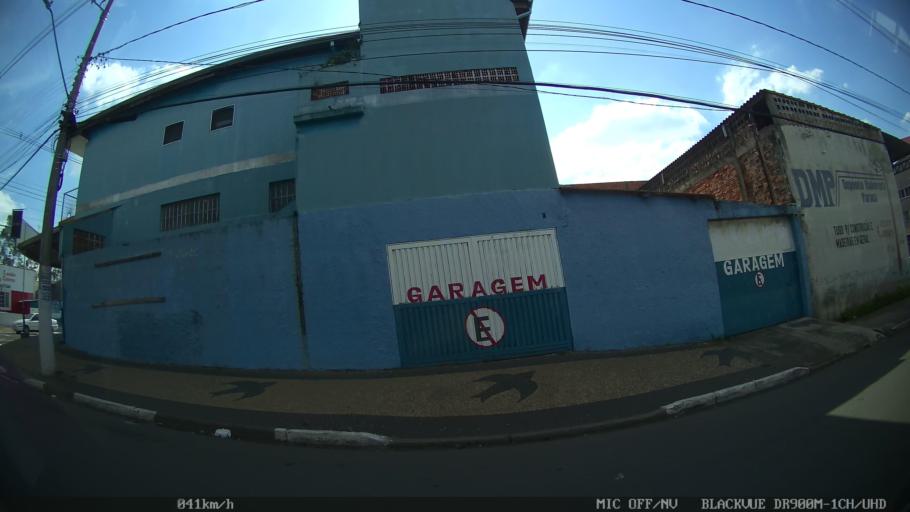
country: BR
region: Sao Paulo
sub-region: Hortolandia
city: Hortolandia
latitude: -22.9049
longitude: -47.2470
